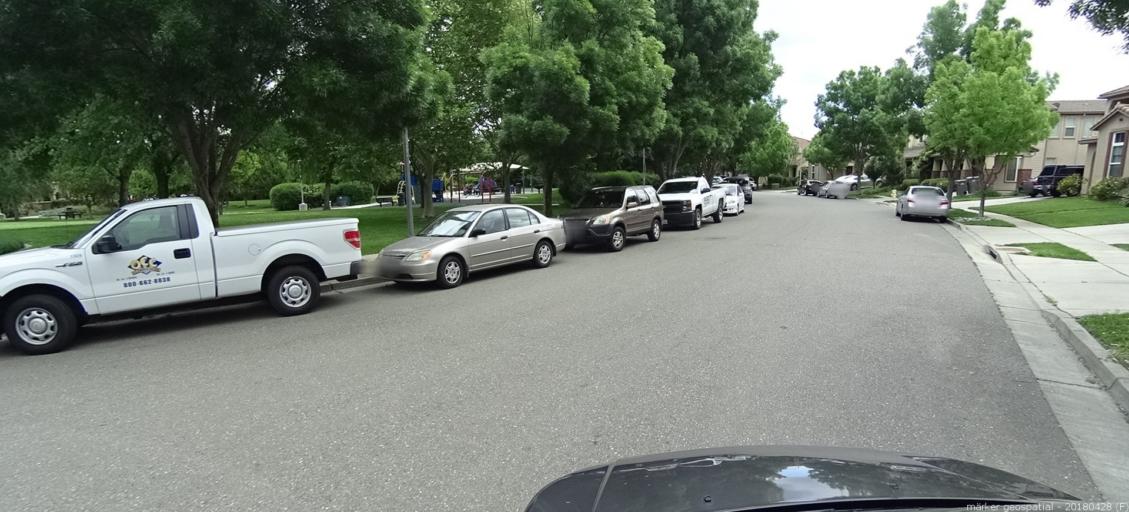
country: US
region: California
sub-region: Yolo County
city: West Sacramento
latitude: 38.5528
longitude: -121.5184
